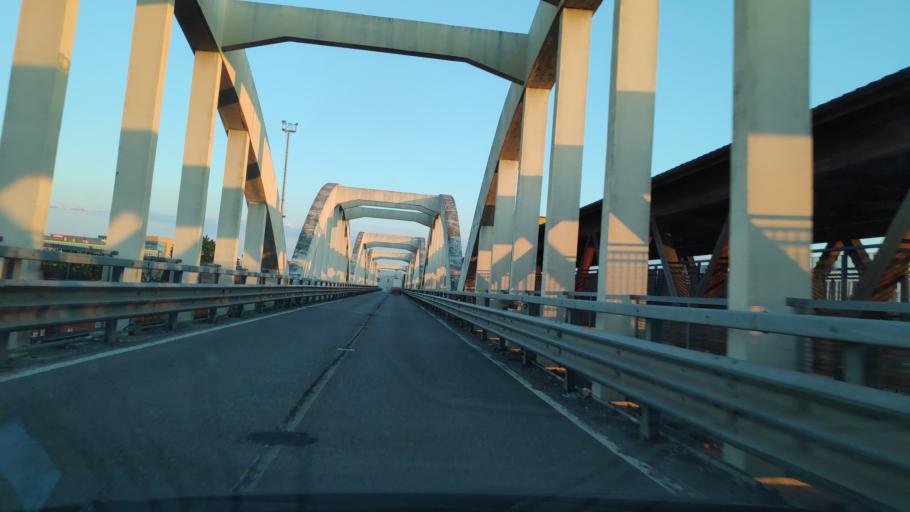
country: IT
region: Lombardy
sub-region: Citta metropolitana di Milano
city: Segrate
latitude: 45.4796
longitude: 9.3009
